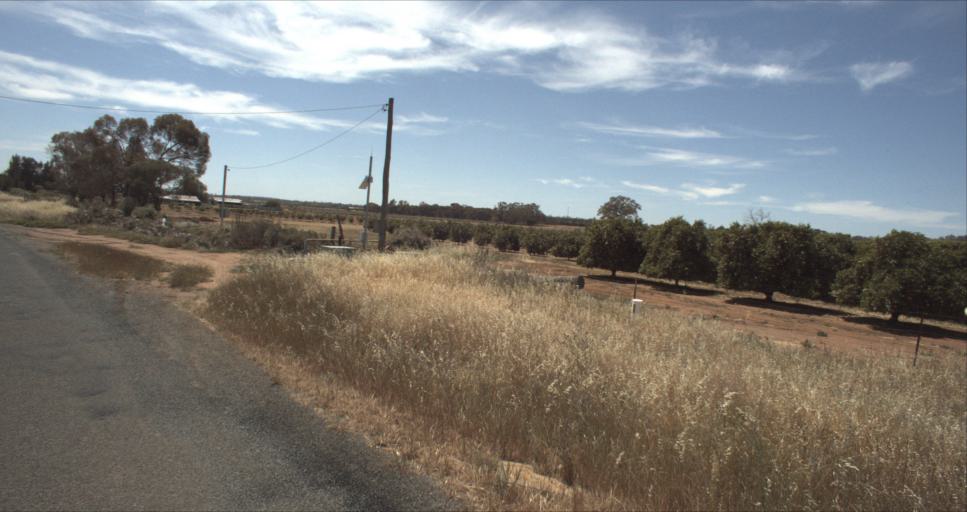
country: AU
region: New South Wales
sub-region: Leeton
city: Leeton
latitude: -34.6087
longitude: 146.4256
